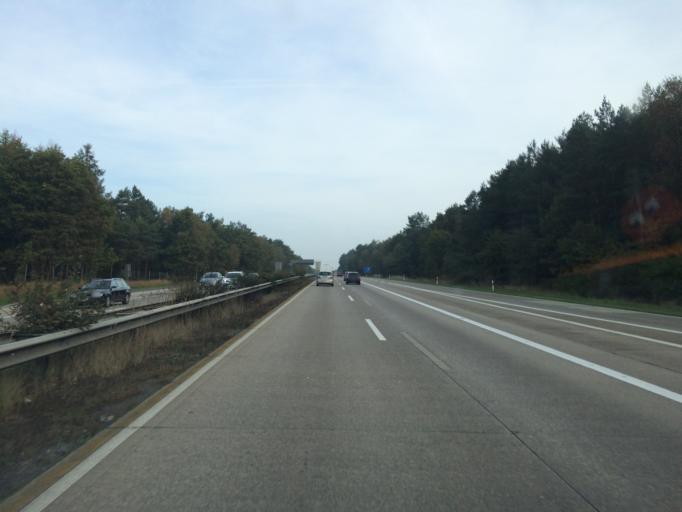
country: DE
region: Lower Saxony
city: Bad Fallingbostel
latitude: 52.7952
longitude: 9.6749
